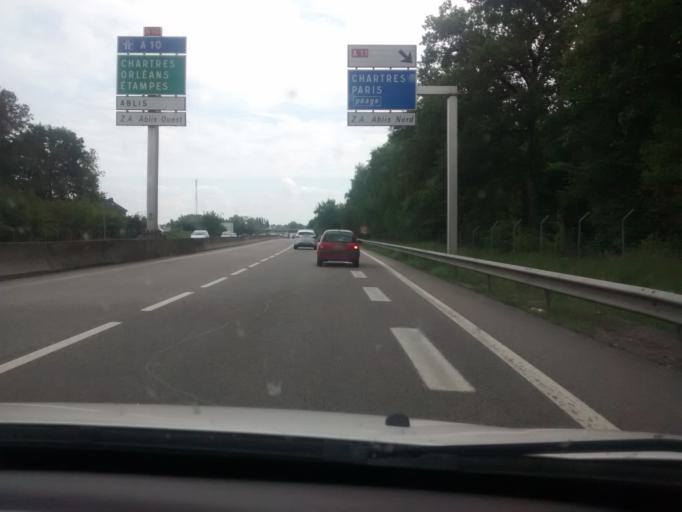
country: FR
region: Ile-de-France
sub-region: Departement des Yvelines
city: Ablis
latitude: 48.5351
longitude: 1.8290
